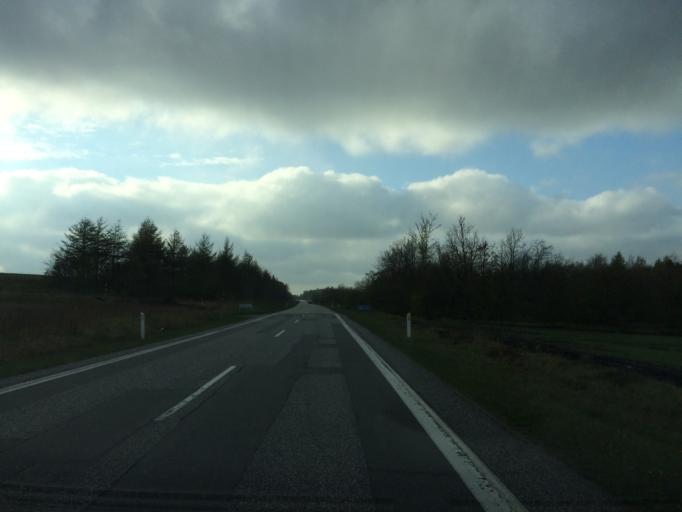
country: DK
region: Central Jutland
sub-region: Viborg Kommune
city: Karup
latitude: 56.3309
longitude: 9.1014
